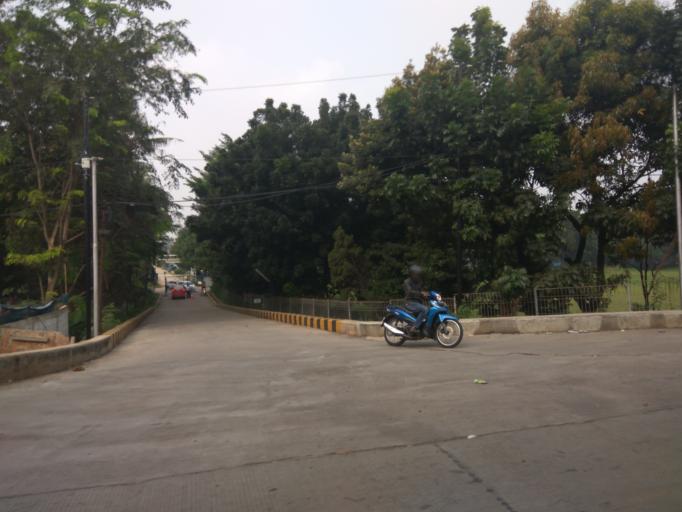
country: ID
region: West Java
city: Bekasi
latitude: -6.2493
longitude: 106.9338
